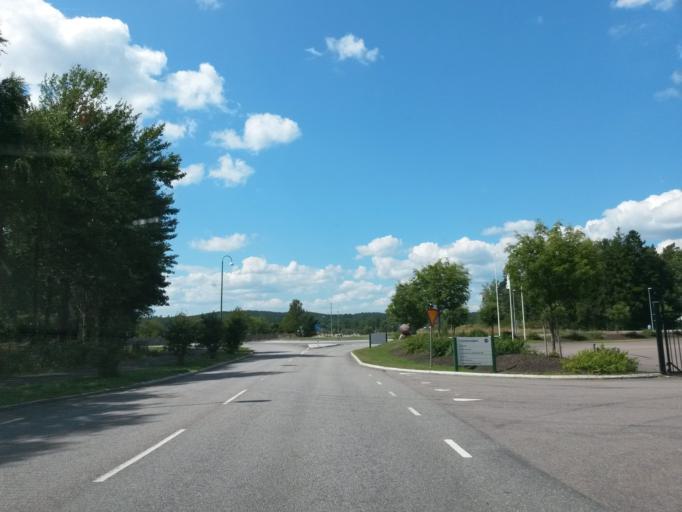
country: SE
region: Vaestra Goetaland
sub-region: Lerums Kommun
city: Stenkullen
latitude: 57.7960
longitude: 12.3093
